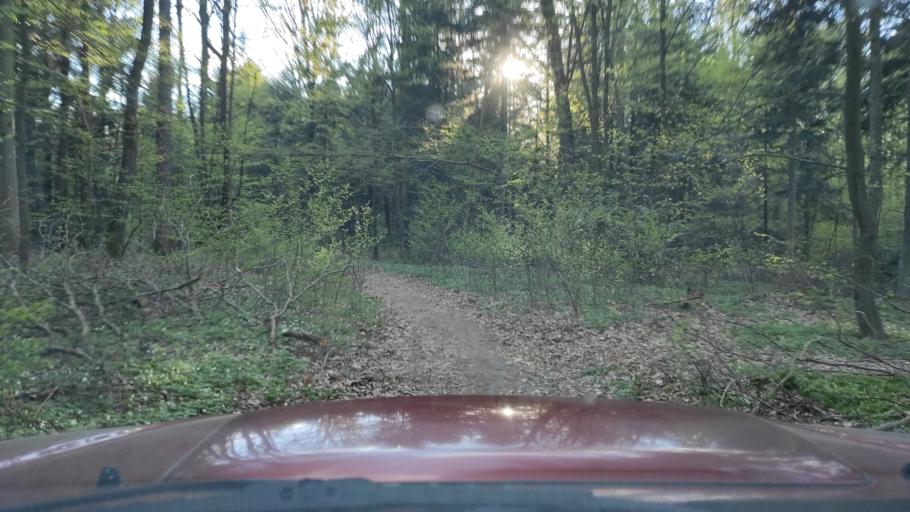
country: PL
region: Masovian Voivodeship
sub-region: Powiat radomski
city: Pionki
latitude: 51.4745
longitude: 21.4348
